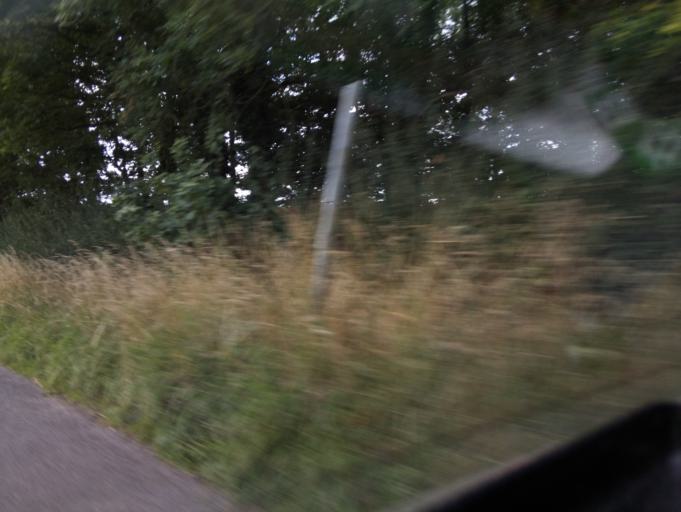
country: GB
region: England
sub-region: Gloucestershire
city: Chalford
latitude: 51.7710
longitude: -2.0910
